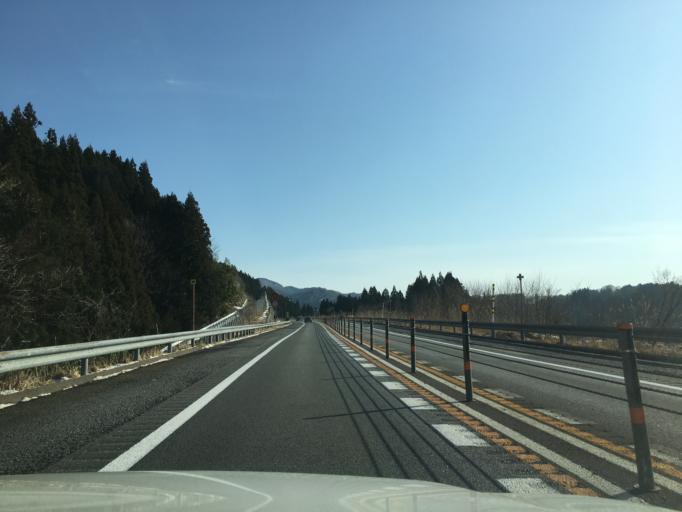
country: JP
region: Yamagata
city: Tsuruoka
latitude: 38.6076
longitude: 139.8427
